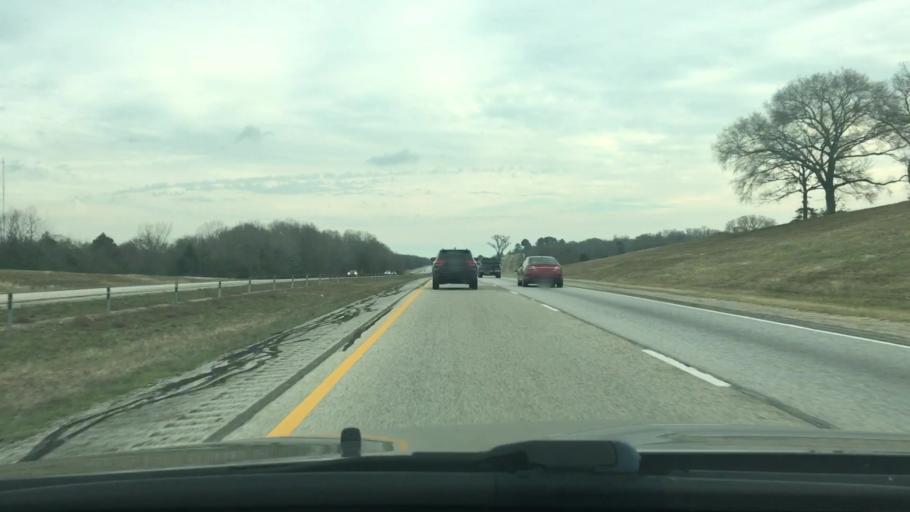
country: US
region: Texas
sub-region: Leon County
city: Centerville
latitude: 31.2872
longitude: -95.9945
